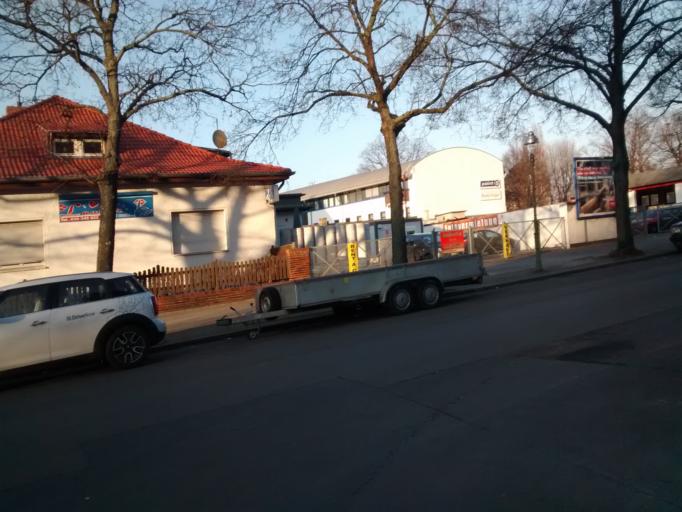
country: DE
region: Berlin
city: Charlottenburg-Nord
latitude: 52.5231
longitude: 13.3145
